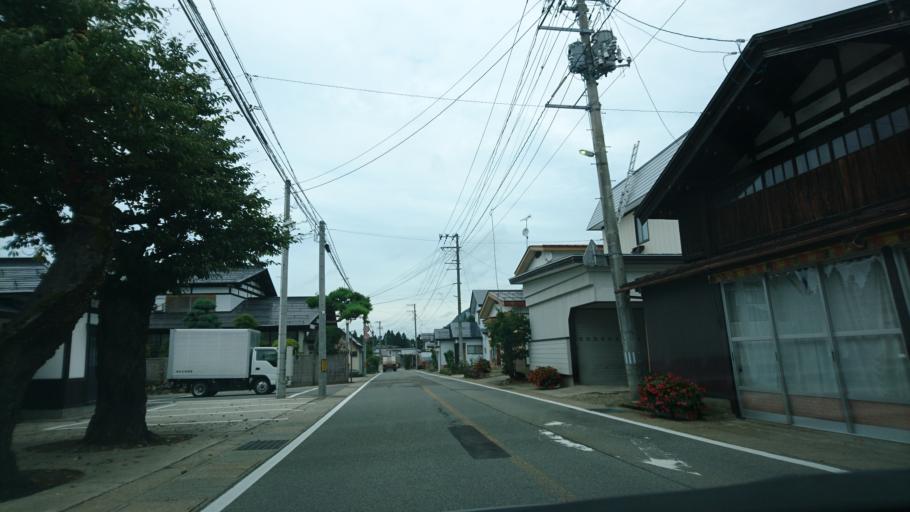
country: JP
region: Akita
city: Yuzawa
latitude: 39.1079
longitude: 140.5828
